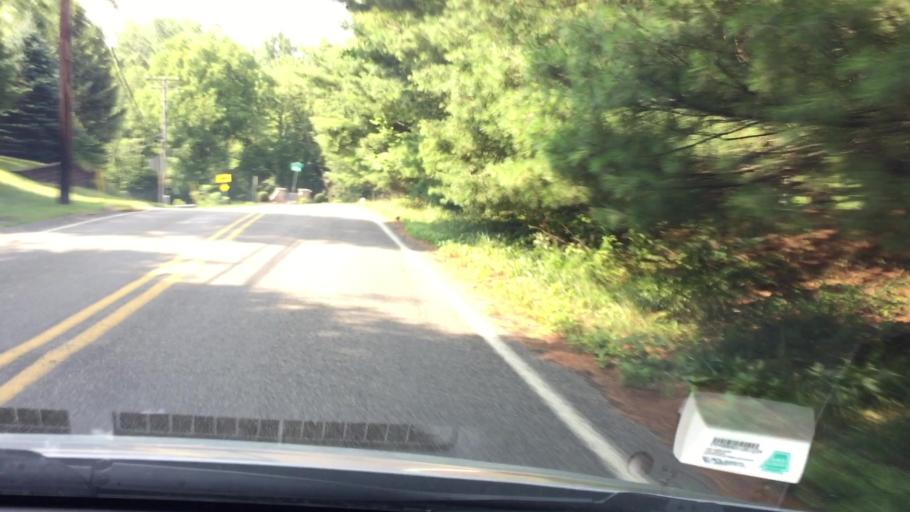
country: US
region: Pennsylvania
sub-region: Allegheny County
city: Franklin Park
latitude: 40.5752
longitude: -80.1205
